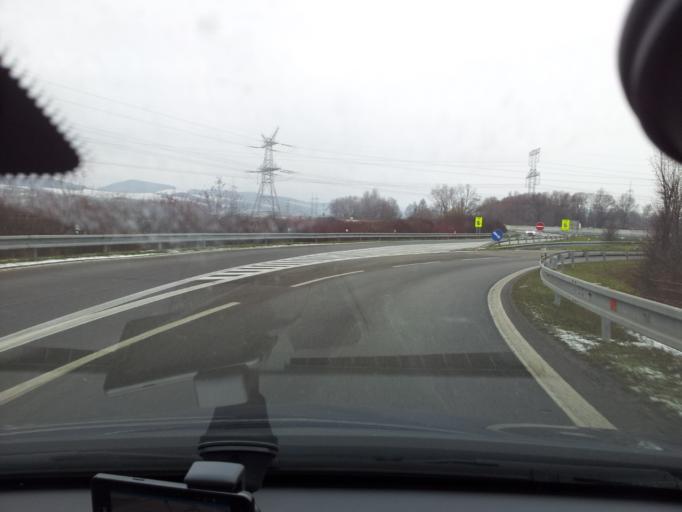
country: SK
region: Kosicky
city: Kosice
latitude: 48.8573
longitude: 21.2667
